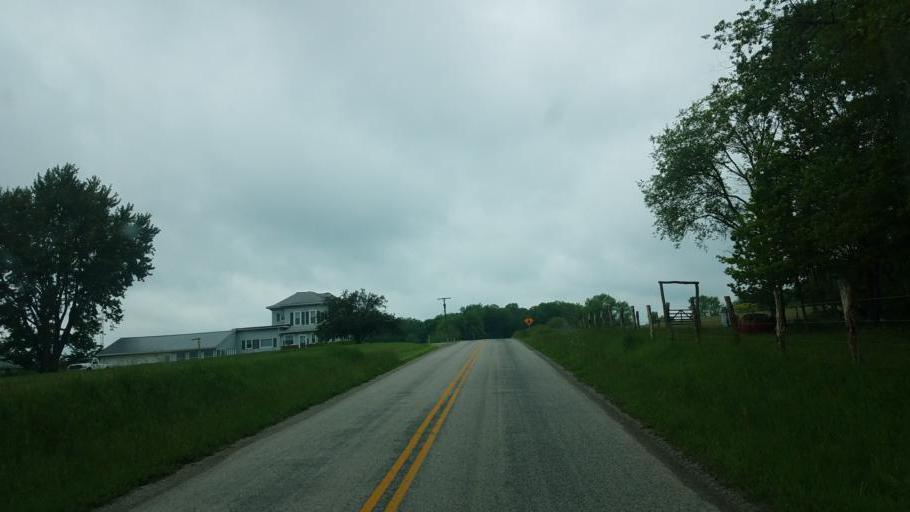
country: US
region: Ohio
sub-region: Ashland County
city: Loudonville
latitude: 40.7330
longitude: -82.3141
